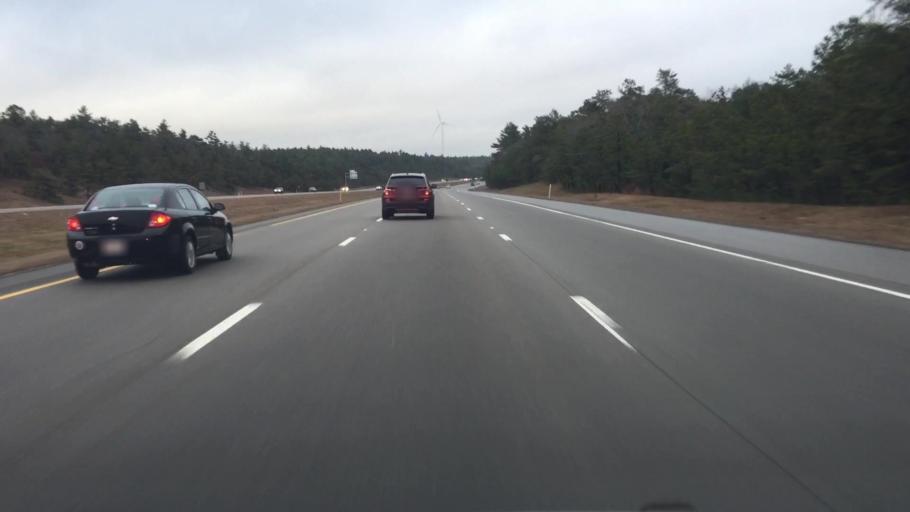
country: US
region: Massachusetts
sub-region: Plymouth County
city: White Island Shores
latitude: 41.7714
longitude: -70.6423
